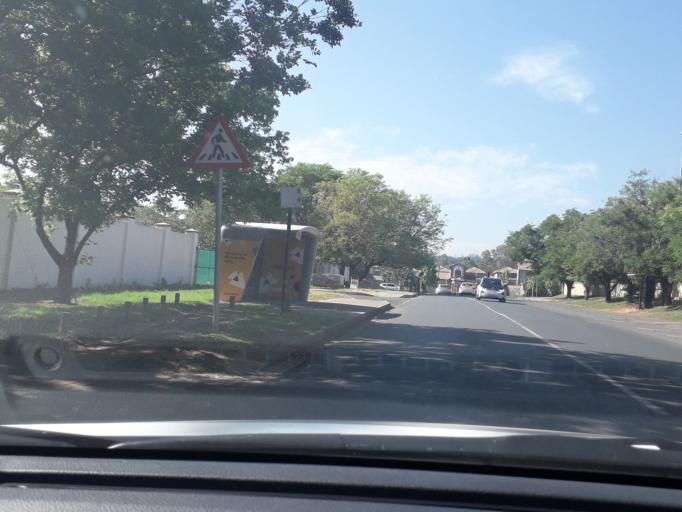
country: ZA
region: Gauteng
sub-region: City of Johannesburg Metropolitan Municipality
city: Midrand
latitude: -26.0730
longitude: 28.0347
